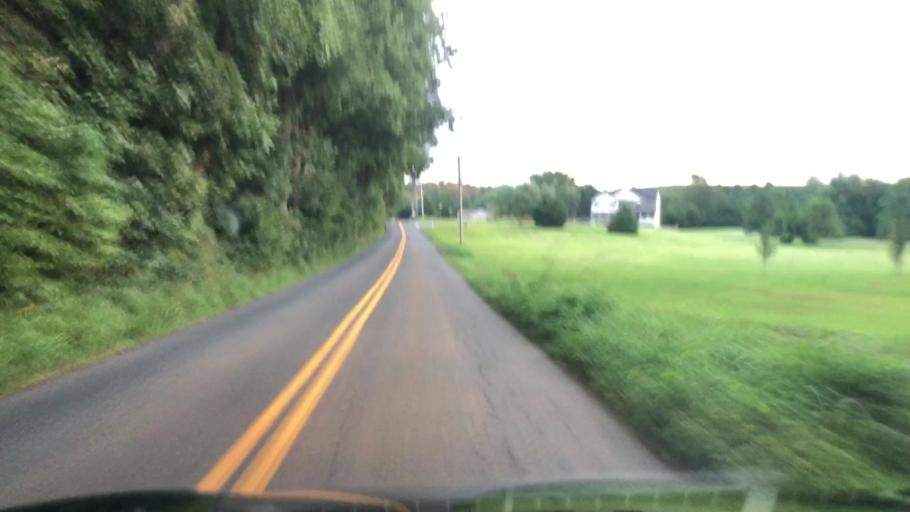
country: US
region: Virginia
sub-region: Stafford County
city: Stafford
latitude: 38.4674
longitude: -77.5789
